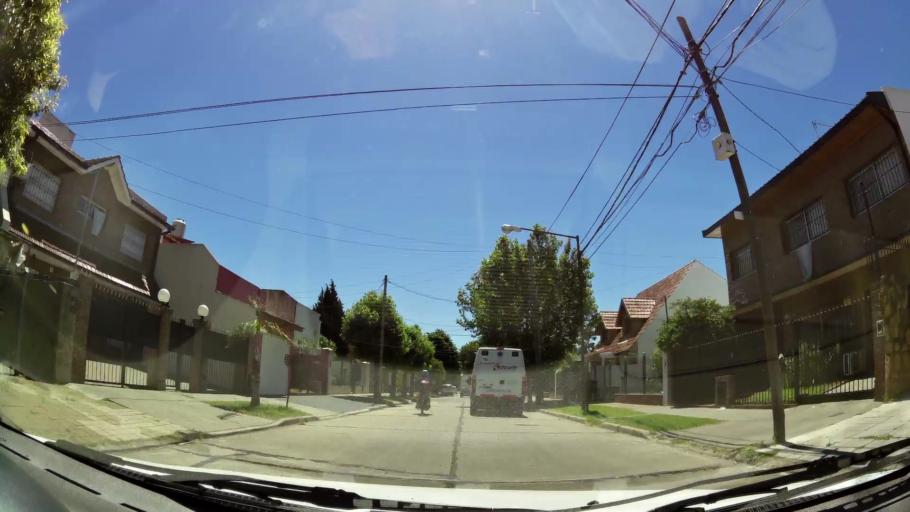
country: AR
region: Buenos Aires
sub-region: Partido de San Isidro
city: San Isidro
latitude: -34.5065
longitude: -58.5462
